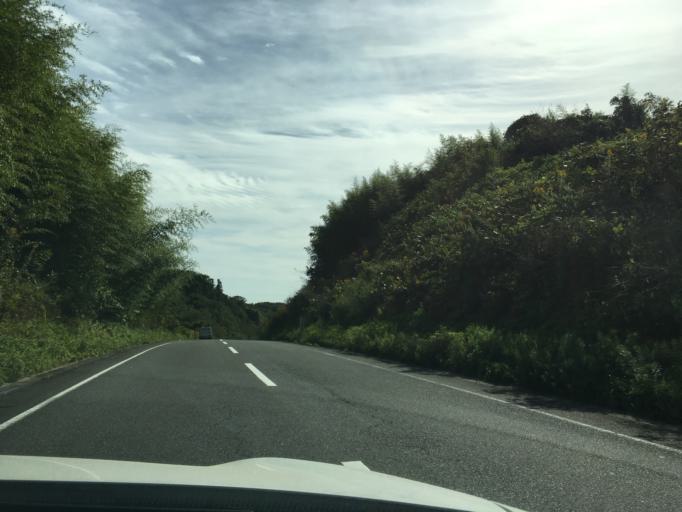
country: JP
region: Fukushima
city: Nihommatsu
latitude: 37.5538
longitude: 140.4995
